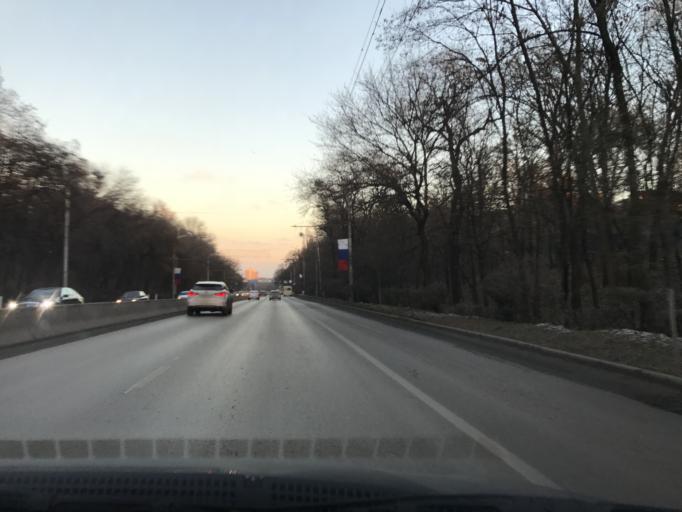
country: RU
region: Rostov
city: Rostov-na-Donu
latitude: 47.2112
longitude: 39.6814
